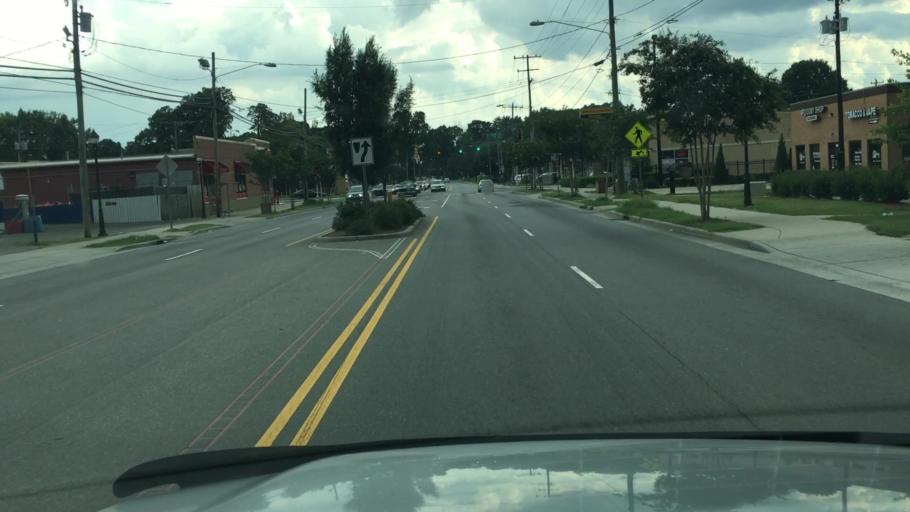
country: US
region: North Carolina
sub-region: Mecklenburg County
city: Charlotte
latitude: 35.2639
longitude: -80.8545
